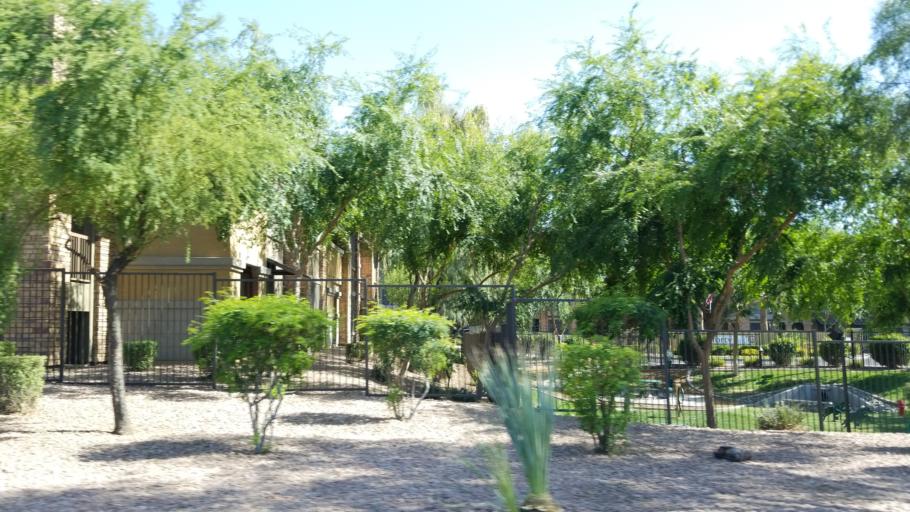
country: US
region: Arizona
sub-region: Maricopa County
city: Tempe Junction
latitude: 33.4656
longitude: -111.9895
